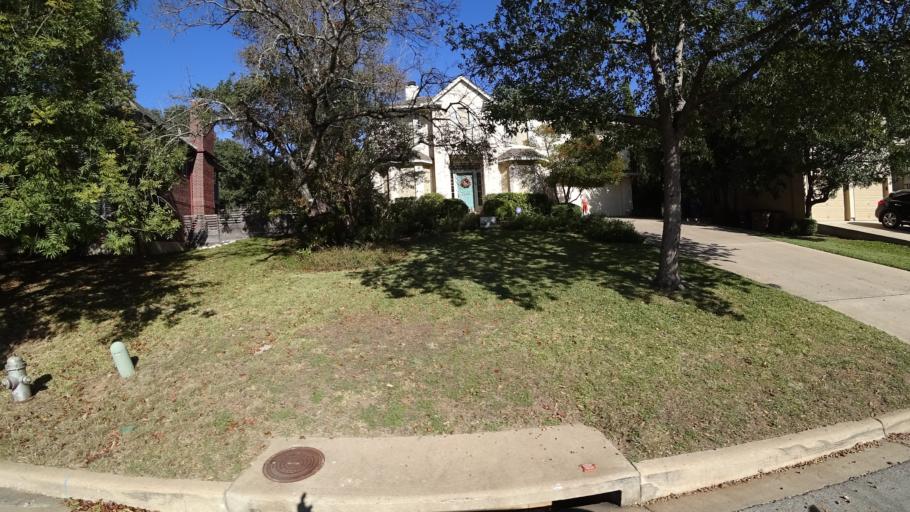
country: US
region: Texas
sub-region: Williamson County
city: Jollyville
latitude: 30.4146
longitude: -97.7717
